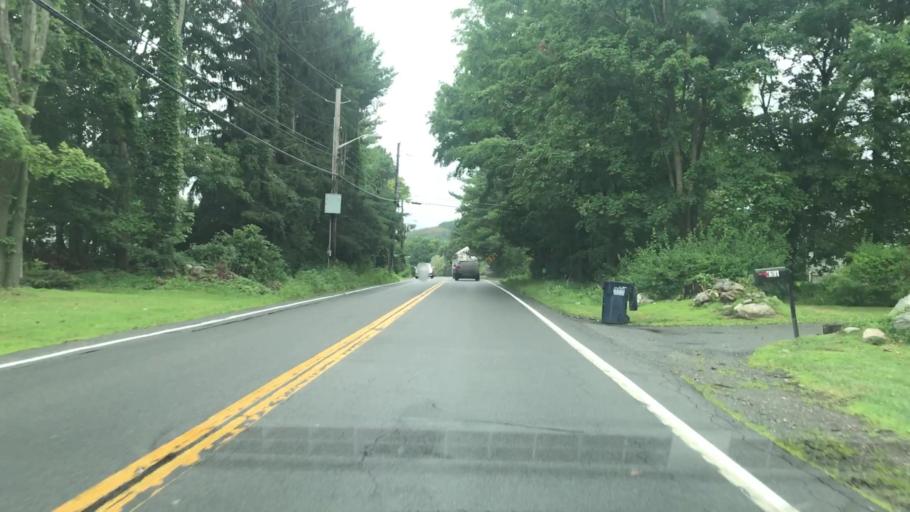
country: US
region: New York
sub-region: Westchester County
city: Jefferson Valley-Yorktown
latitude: 41.3504
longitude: -73.7803
